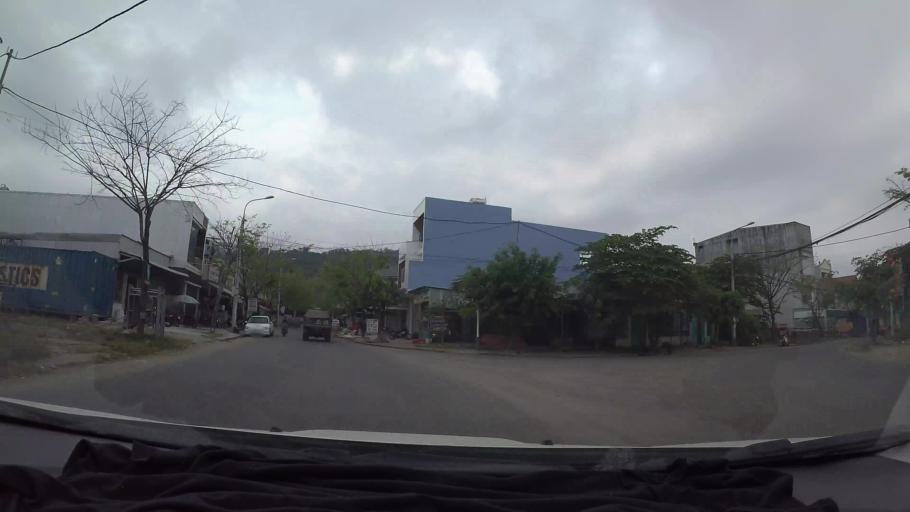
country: VN
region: Da Nang
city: Thanh Khe
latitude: 16.0431
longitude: 108.1729
